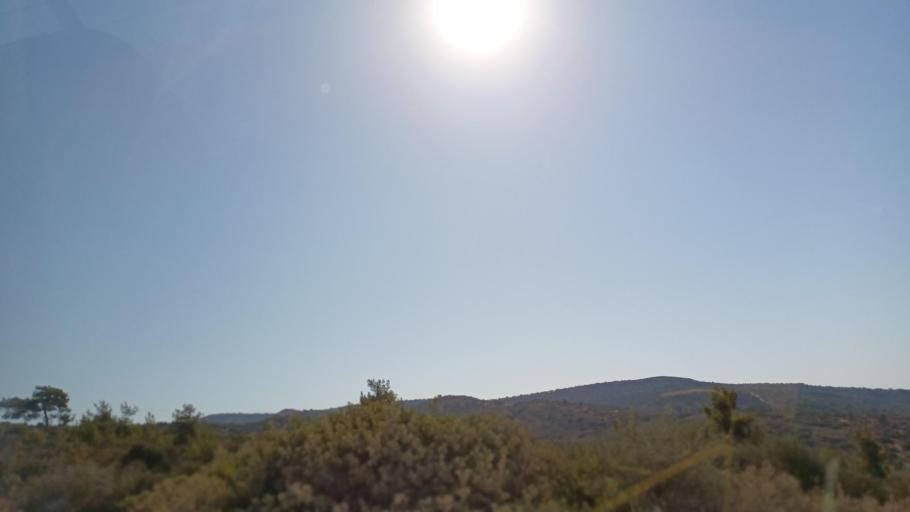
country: CY
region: Limassol
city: Pissouri
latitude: 34.7237
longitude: 32.6791
